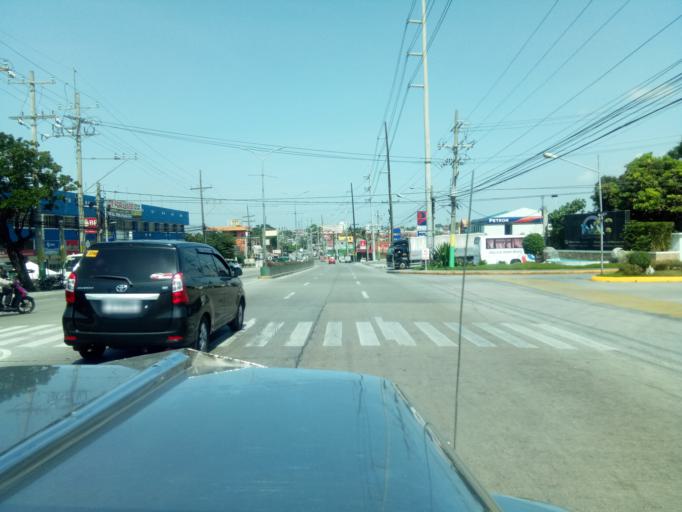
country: PH
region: Calabarzon
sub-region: Province of Cavite
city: Manggahan
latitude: 14.2920
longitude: 120.9327
